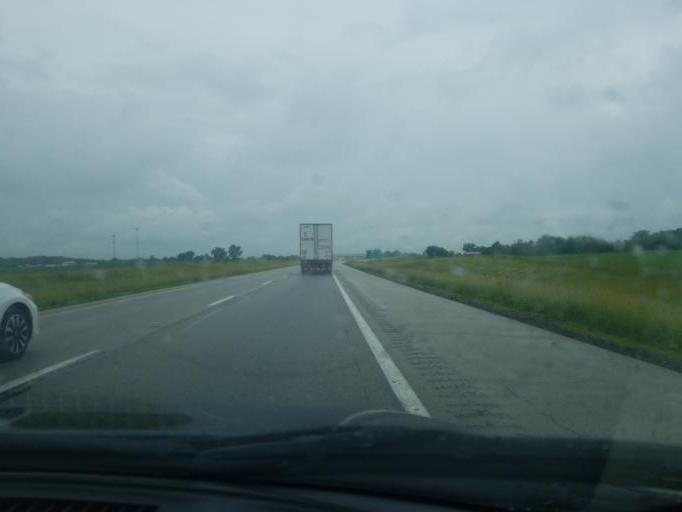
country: US
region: Ohio
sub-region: Greene County
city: Jamestown
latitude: 39.5614
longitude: -83.7128
